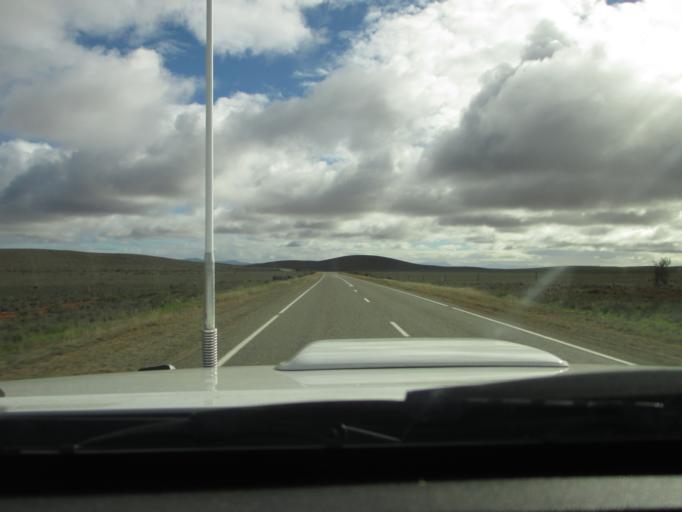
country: AU
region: South Australia
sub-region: Flinders Ranges
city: Quorn
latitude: -32.1657
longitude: 138.5340
